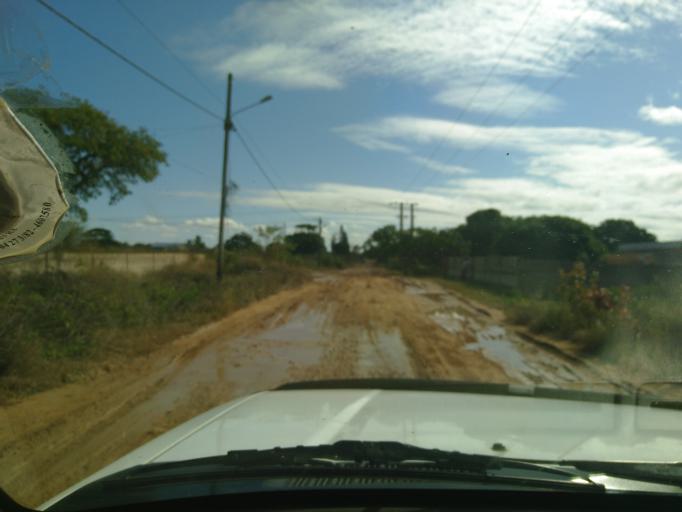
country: MZ
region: Maputo City
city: Maputo
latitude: -25.9946
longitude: 32.5369
